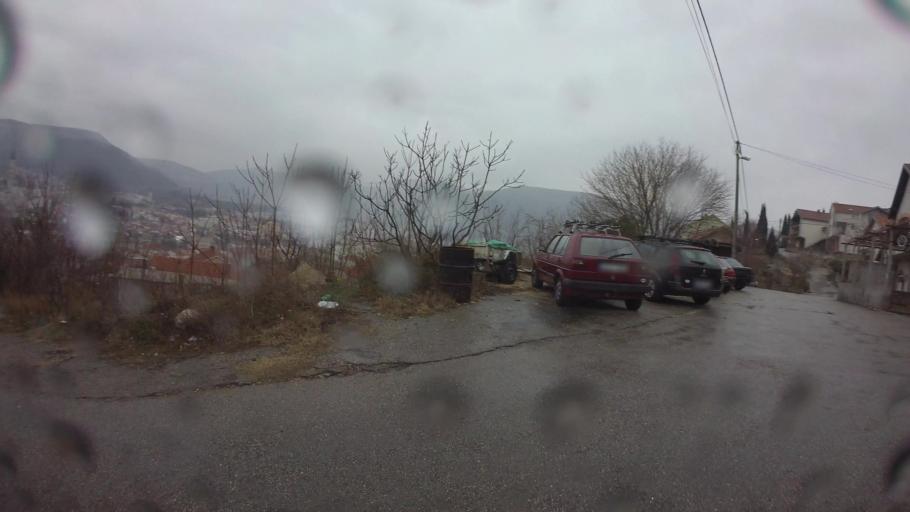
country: BA
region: Federation of Bosnia and Herzegovina
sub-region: Hercegovacko-Bosanski Kanton
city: Mostar
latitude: 43.3413
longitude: 17.8197
